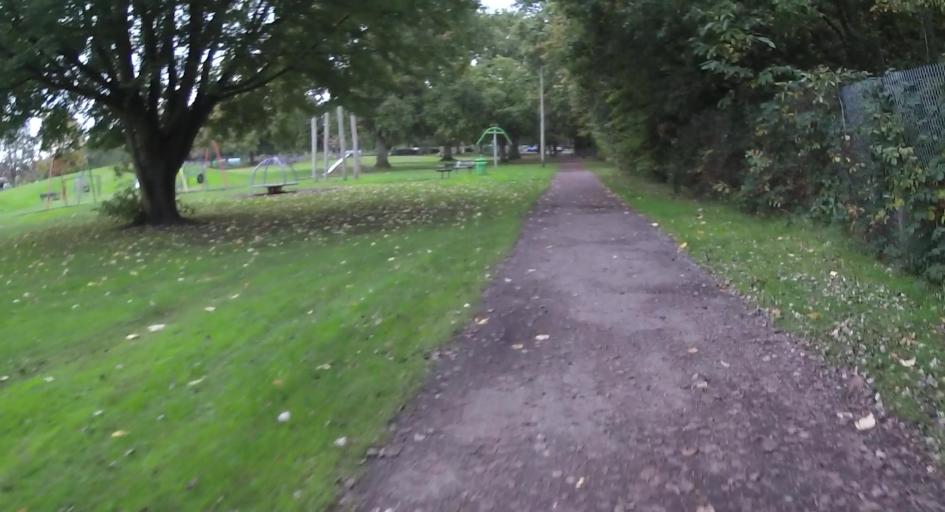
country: GB
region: England
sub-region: Bracknell Forest
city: Crowthorne
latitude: 51.3955
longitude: -0.7799
